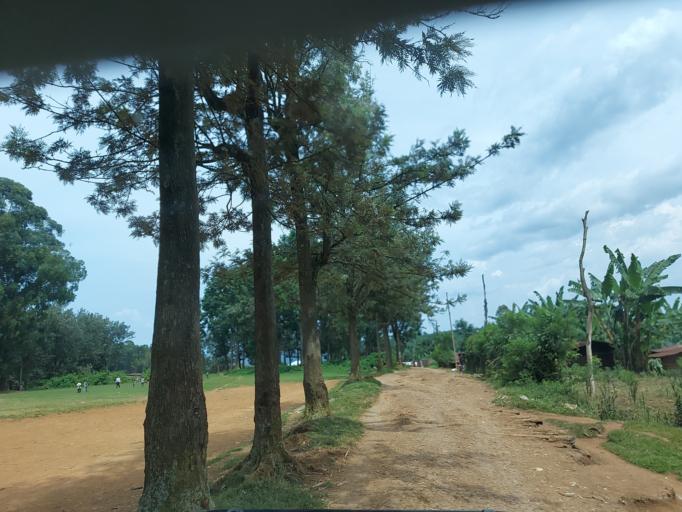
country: RW
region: Western Province
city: Cyangugu
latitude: -2.2346
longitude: 28.8541
